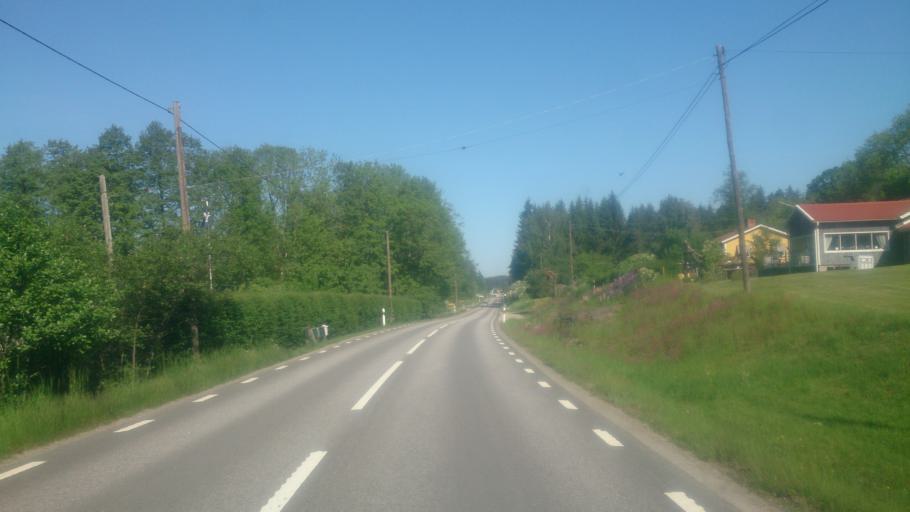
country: SE
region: OEstergoetland
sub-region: Atvidabergs Kommun
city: Atvidaberg
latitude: 58.1042
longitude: 16.1139
